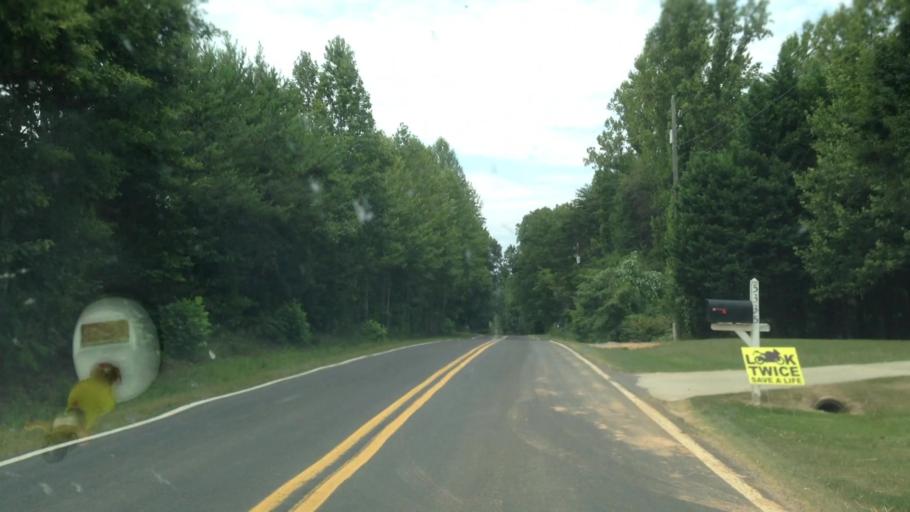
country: US
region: North Carolina
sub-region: Forsyth County
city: Walkertown
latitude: 36.2073
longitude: -80.1089
